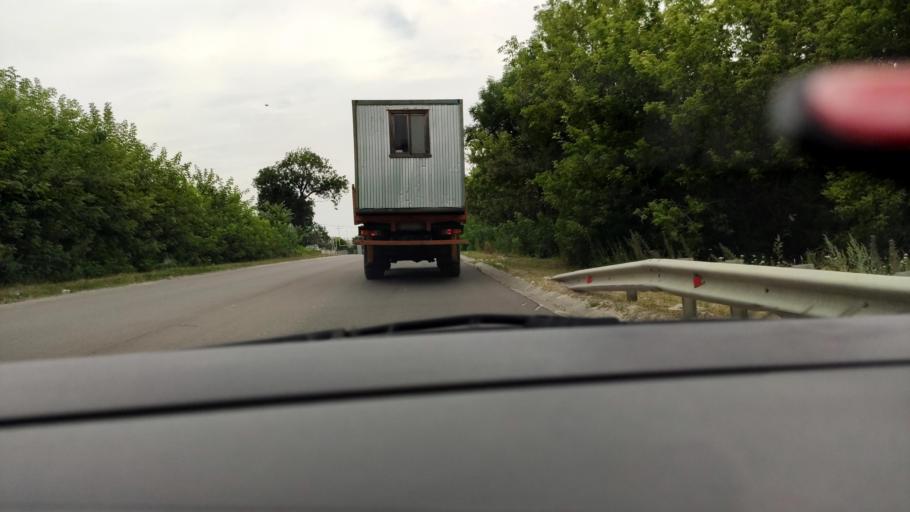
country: RU
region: Voronezj
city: Ramon'
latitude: 51.9041
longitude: 39.3332
